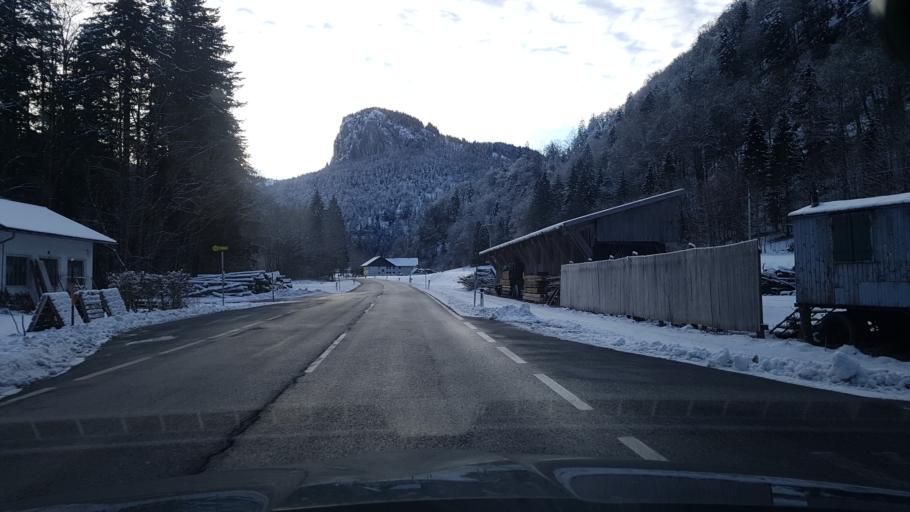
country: AT
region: Salzburg
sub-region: Politischer Bezirk Salzburg-Umgebung
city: Hintersee
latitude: 47.7222
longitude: 13.2789
